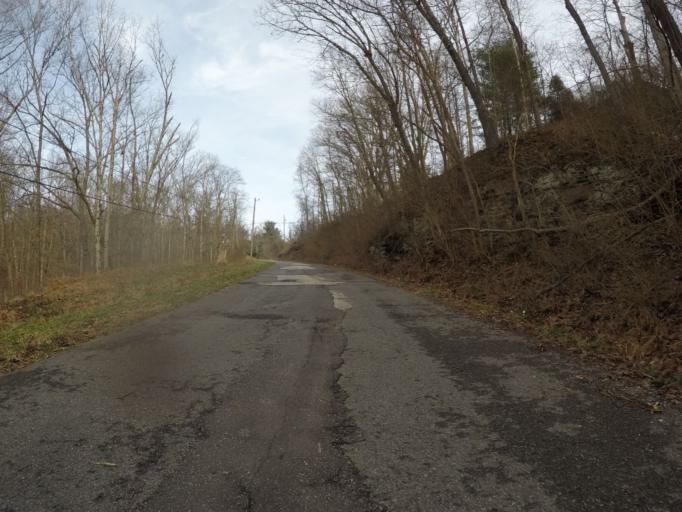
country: US
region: West Virginia
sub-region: Wayne County
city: Lavalette
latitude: 38.3433
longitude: -82.3754
